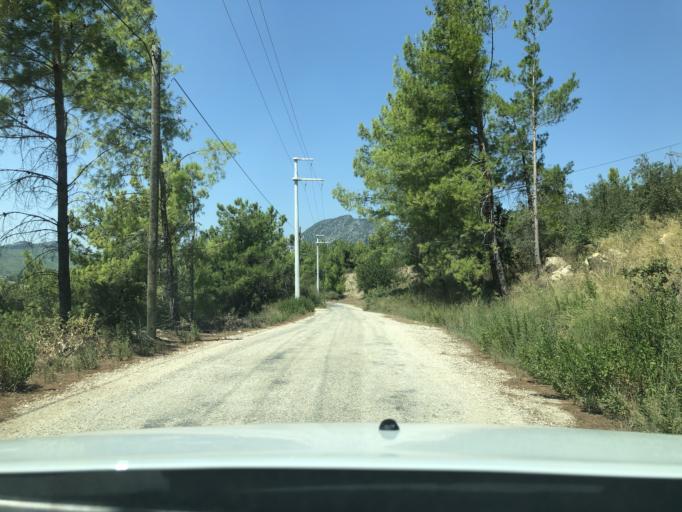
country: TR
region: Antalya
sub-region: Manavgat
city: Manavgat
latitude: 36.8722
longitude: 31.5517
